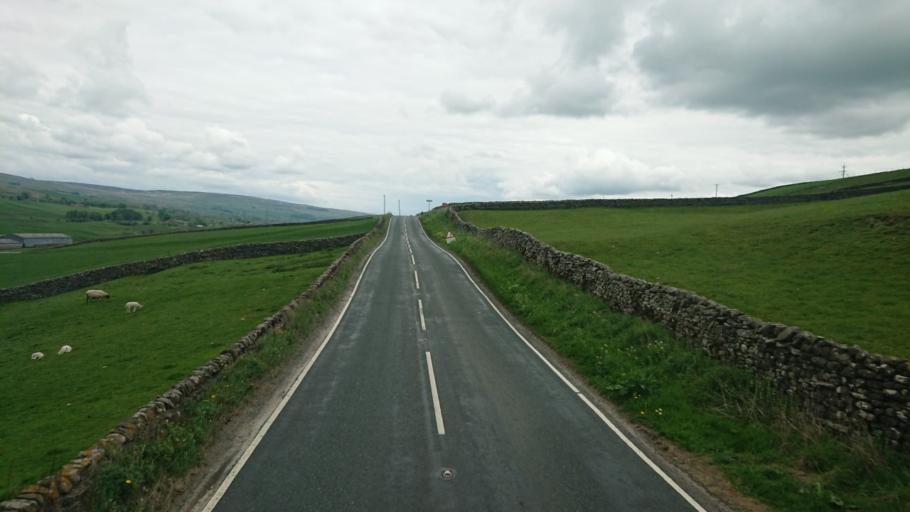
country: GB
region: England
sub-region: Cumbria
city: Kirkby Stephen
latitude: 54.3024
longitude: -2.1606
